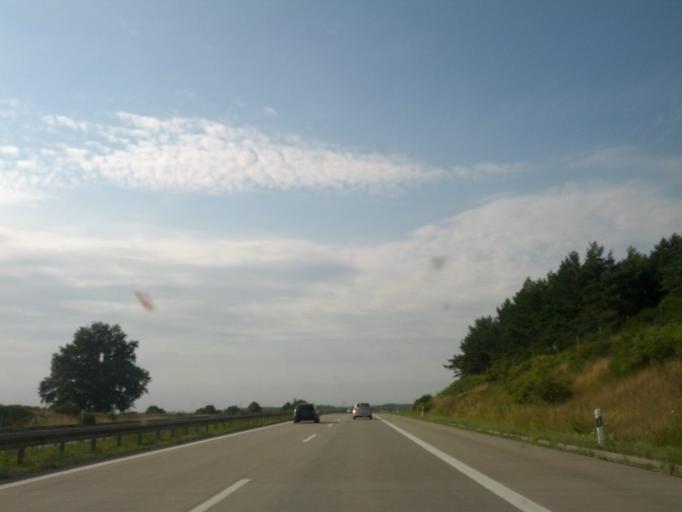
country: DE
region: Mecklenburg-Vorpommern
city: Kavelstorf
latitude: 53.9367
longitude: 12.2158
